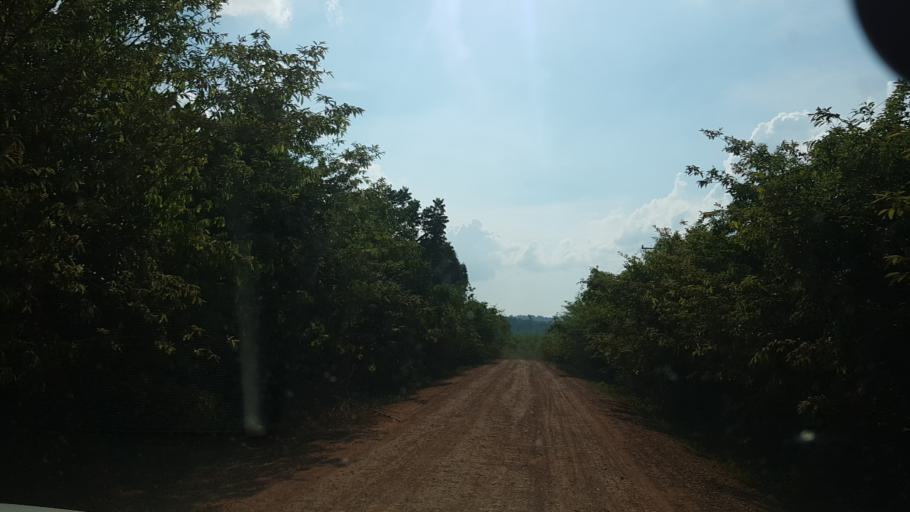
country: LA
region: Vientiane
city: Muang Phon-Hong
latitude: 18.3438
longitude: 102.2934
